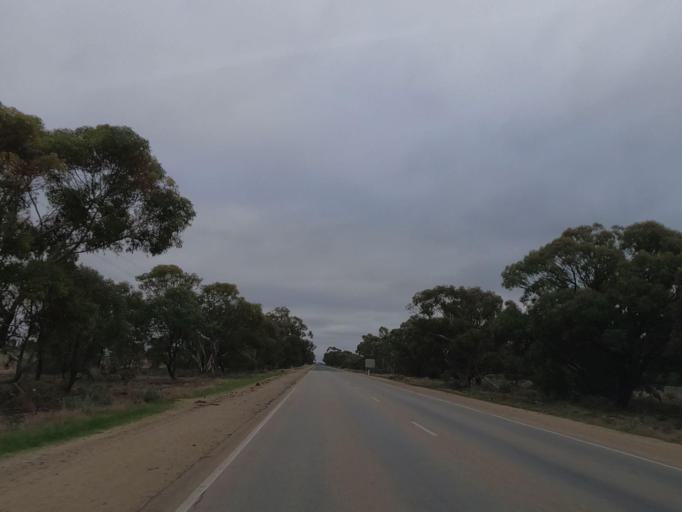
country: AU
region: Victoria
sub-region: Swan Hill
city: Swan Hill
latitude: -35.4021
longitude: 143.5783
